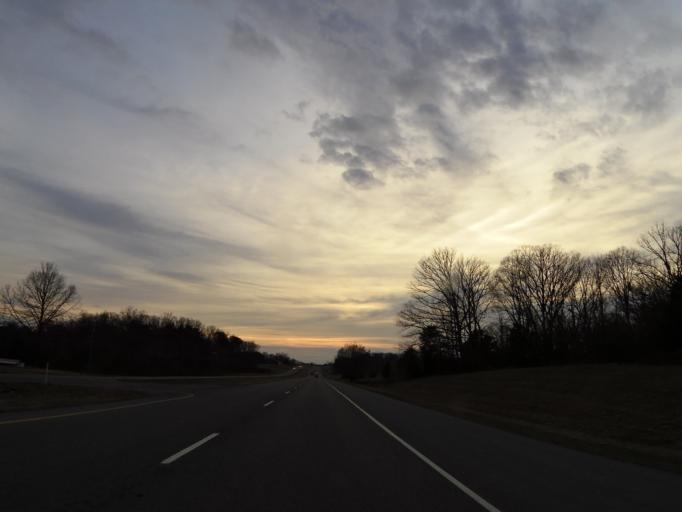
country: US
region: Tennessee
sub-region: Monroe County
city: Madisonville
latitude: 35.4751
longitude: -84.4118
